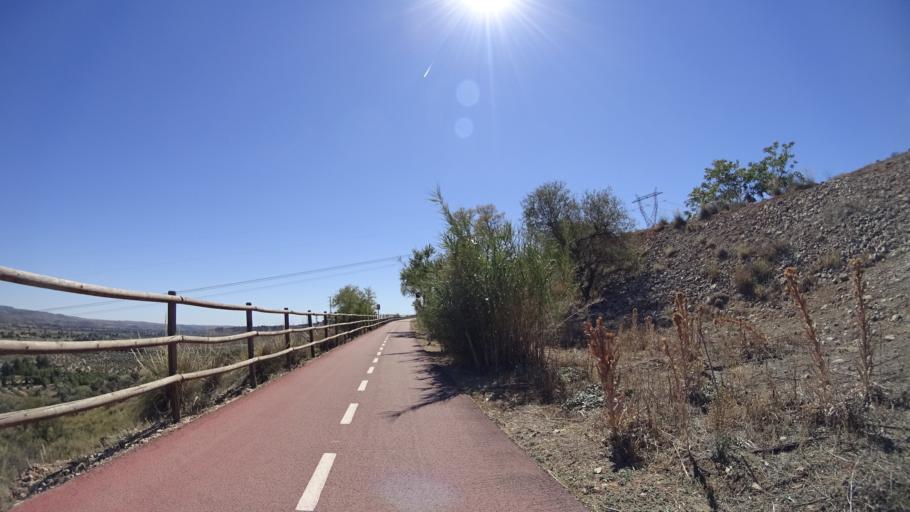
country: ES
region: Madrid
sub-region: Provincia de Madrid
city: Morata de Tajuna
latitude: 40.2318
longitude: -3.4589
